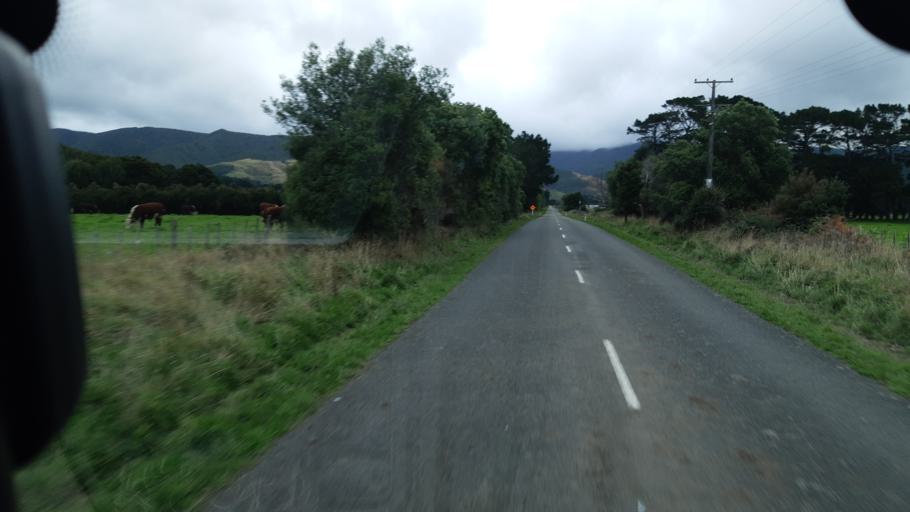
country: NZ
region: Manawatu-Wanganui
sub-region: Palmerston North City
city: Palmerston North
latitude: -40.5750
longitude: 175.6479
